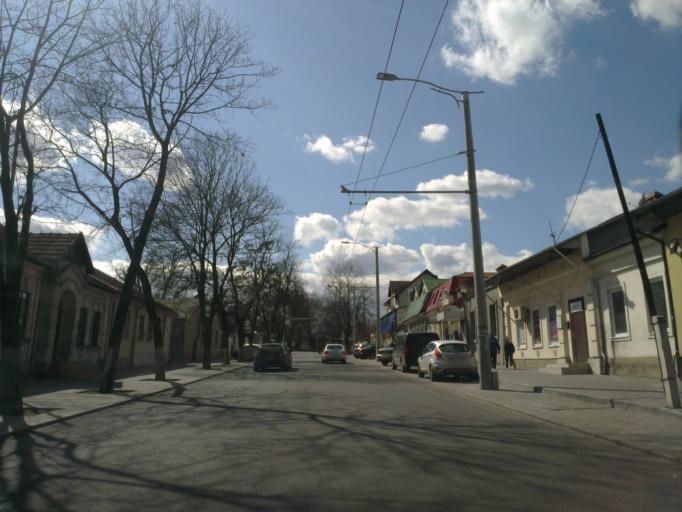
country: MD
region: Chisinau
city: Chisinau
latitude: 47.0150
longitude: 28.8297
